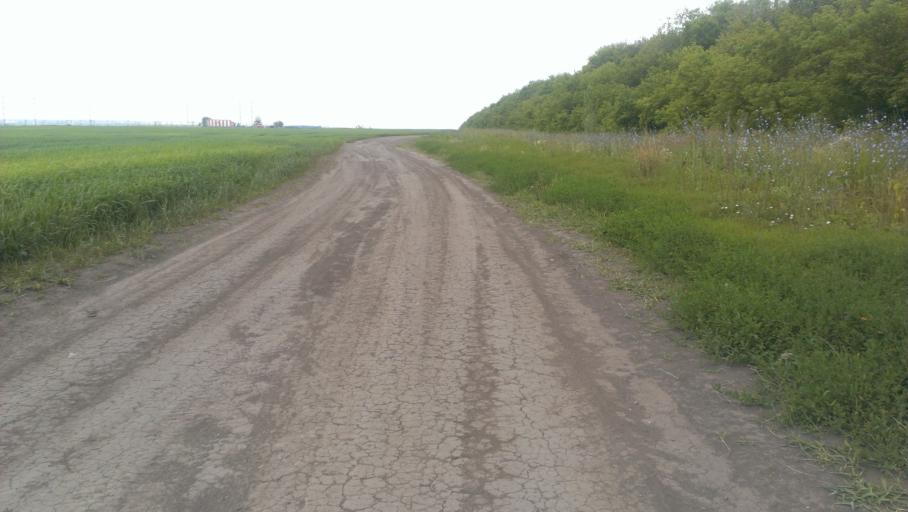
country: RU
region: Altai Krai
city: Gon'ba
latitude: 53.3829
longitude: 83.6199
